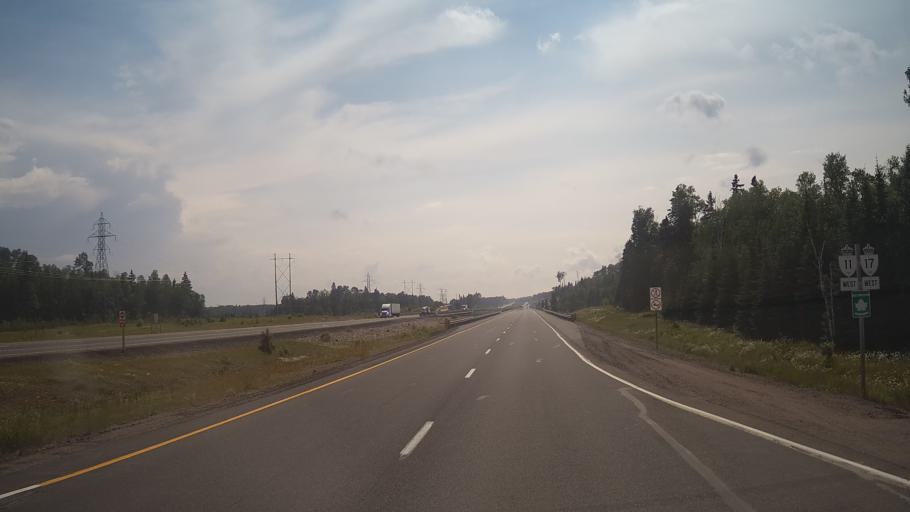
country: CA
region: Ontario
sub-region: Thunder Bay District
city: Thunder Bay
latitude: 48.5406
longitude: -88.9346
